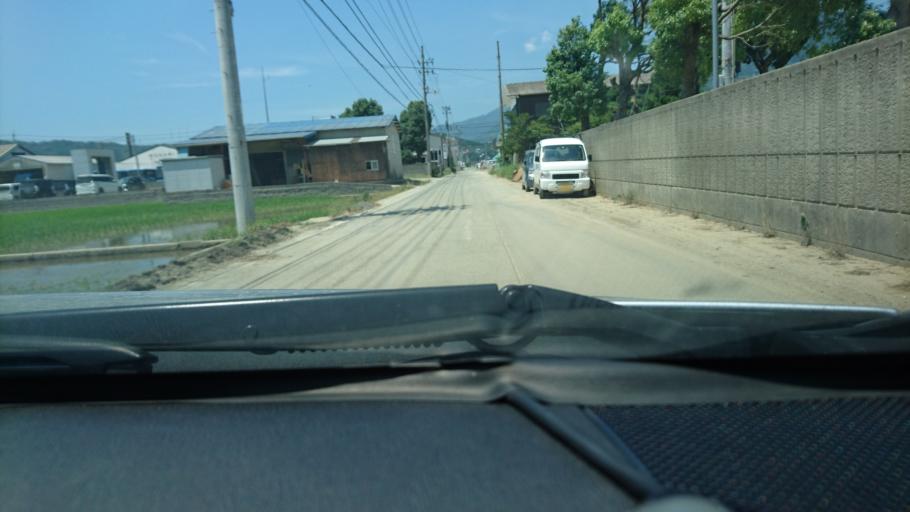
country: JP
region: Ehime
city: Ozu
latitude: 33.5276
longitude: 132.5694
